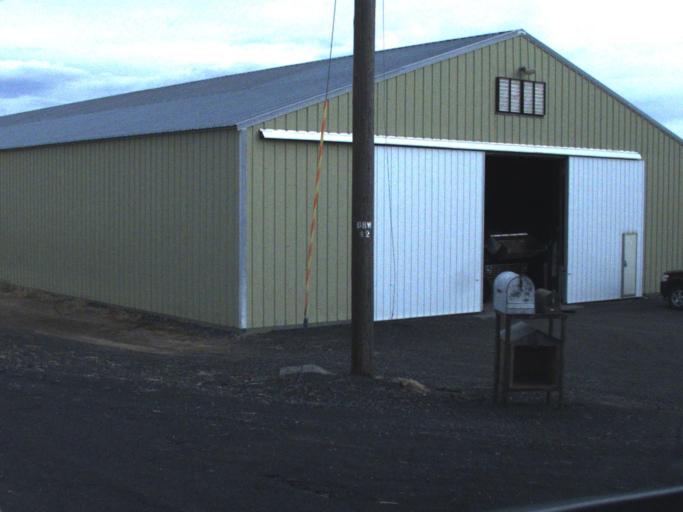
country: US
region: Washington
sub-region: Okanogan County
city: Coulee Dam
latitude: 47.6074
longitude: -118.7861
